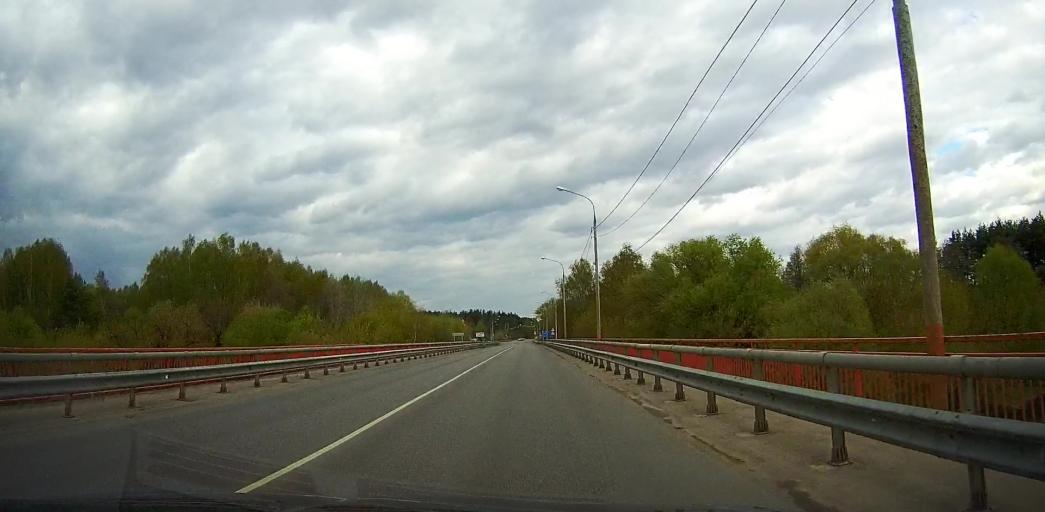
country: RU
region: Moskovskaya
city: Pavlovskiy Posad
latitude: 55.7977
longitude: 38.6527
